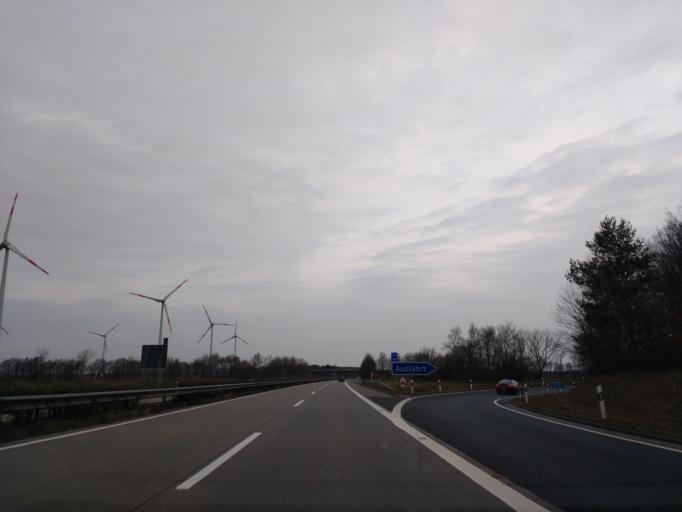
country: DE
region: Lower Saxony
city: Midlum
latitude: 53.6784
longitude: 8.6579
